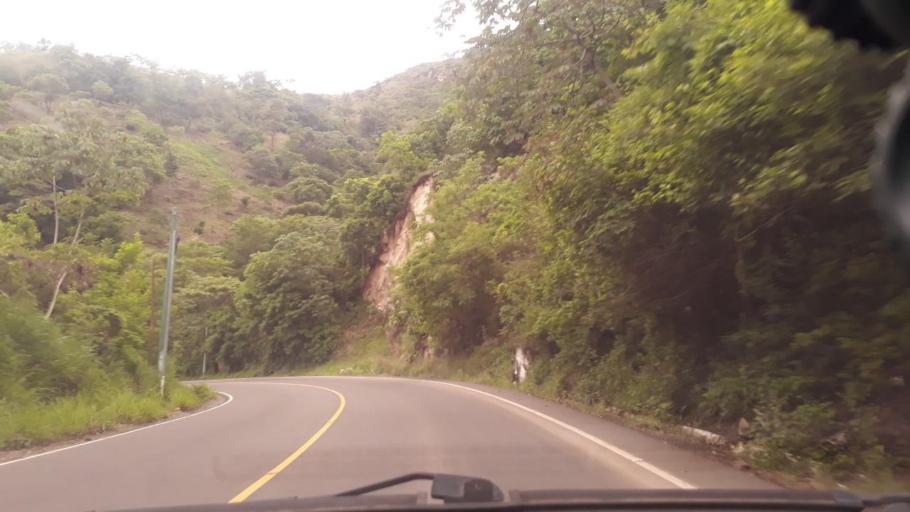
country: GT
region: Chiquimula
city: Quezaltepeque
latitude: 14.6249
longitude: -89.4718
